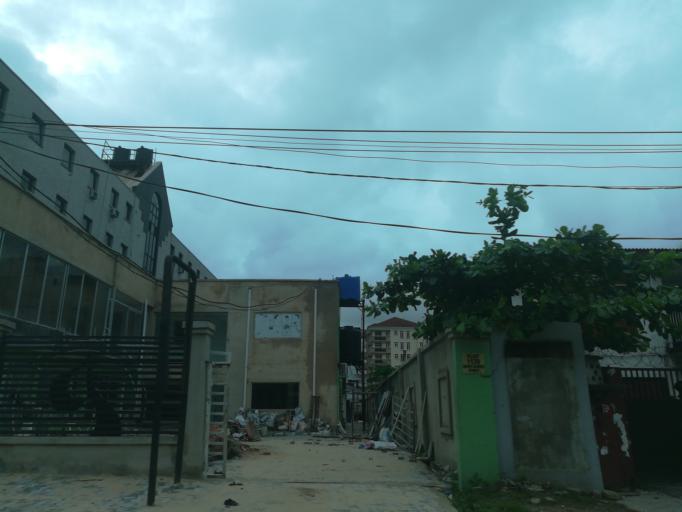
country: NG
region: Lagos
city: Ikoyi
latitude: 6.4239
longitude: 3.4186
